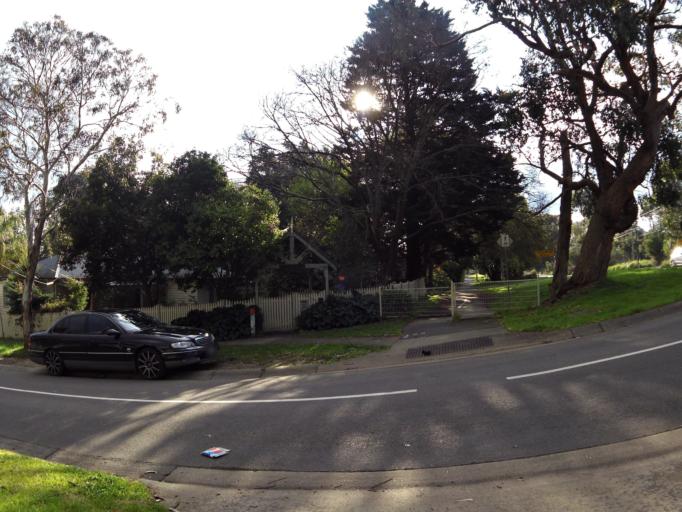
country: AU
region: Victoria
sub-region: Knox
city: The Basin
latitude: -37.8524
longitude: 145.3105
